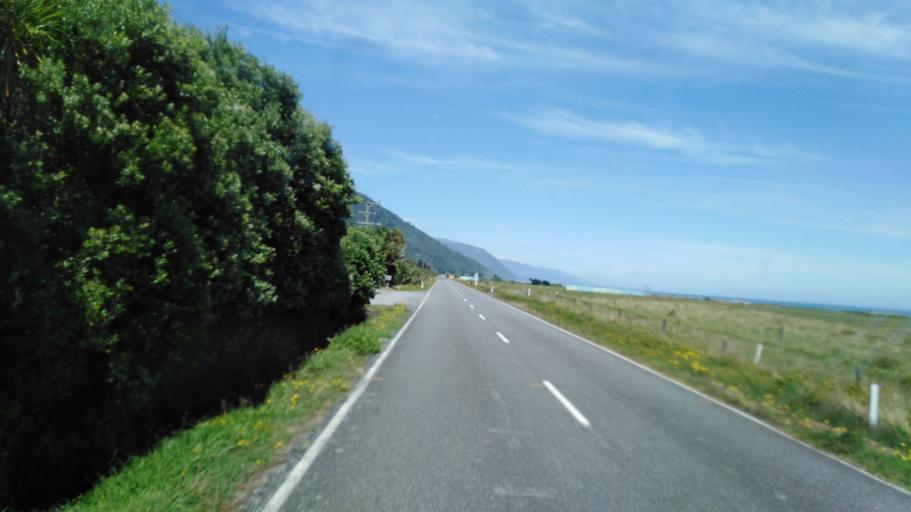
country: NZ
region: West Coast
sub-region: Buller District
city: Westport
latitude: -41.5418
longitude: 171.9278
